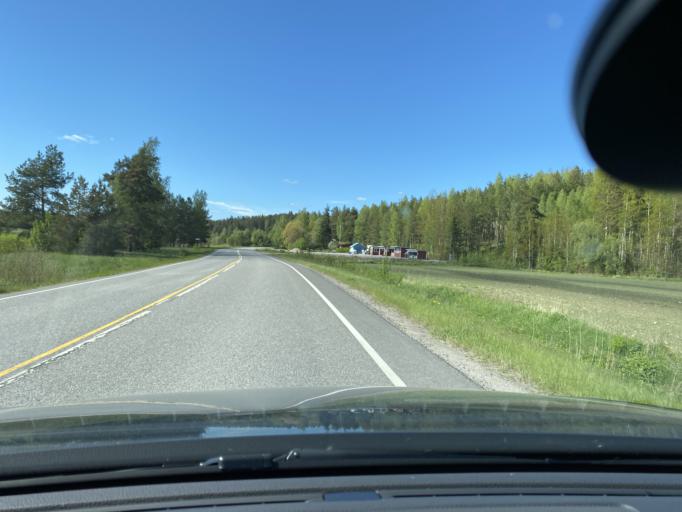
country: FI
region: Varsinais-Suomi
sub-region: Turku
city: Sauvo
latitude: 60.3689
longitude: 22.6733
